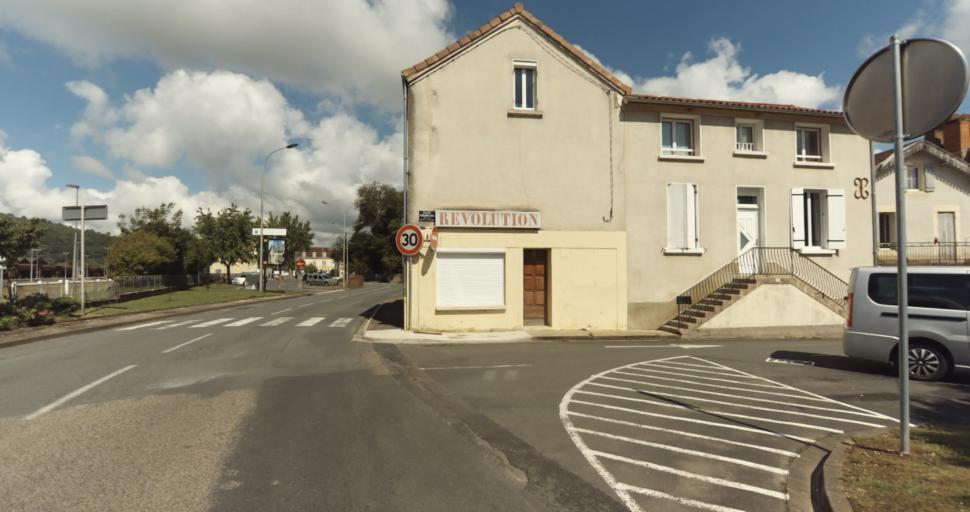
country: FR
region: Aquitaine
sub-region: Departement de la Dordogne
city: Le Bugue
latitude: 44.8468
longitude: 0.9099
